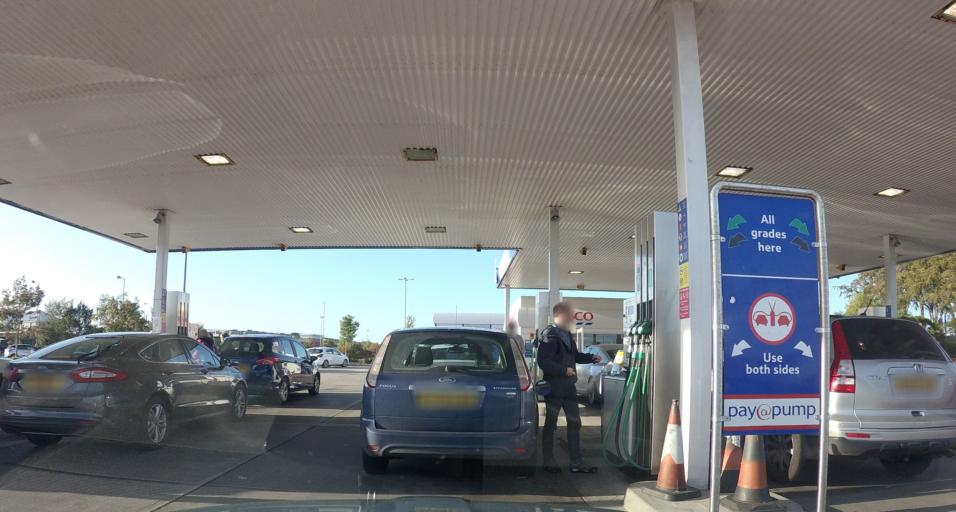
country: GB
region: Scotland
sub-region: Aberdeenshire
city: Westhill
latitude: 57.1479
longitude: -2.2733
